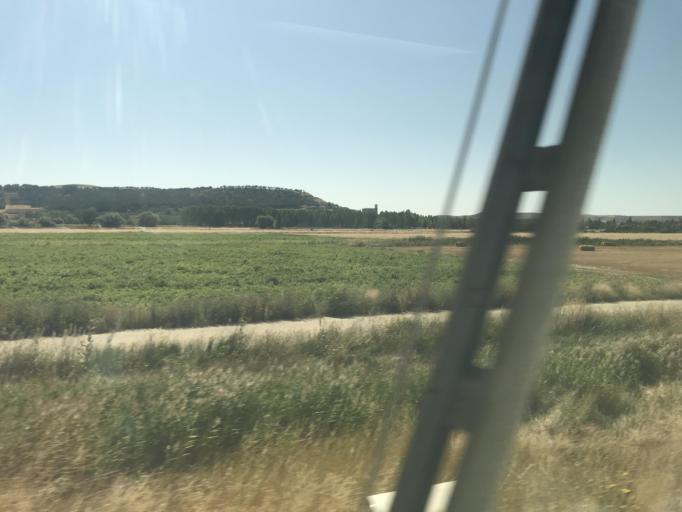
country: ES
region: Castille and Leon
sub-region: Provincia de Burgos
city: Villaquiran de los Infantes
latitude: 42.2192
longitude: -3.9957
